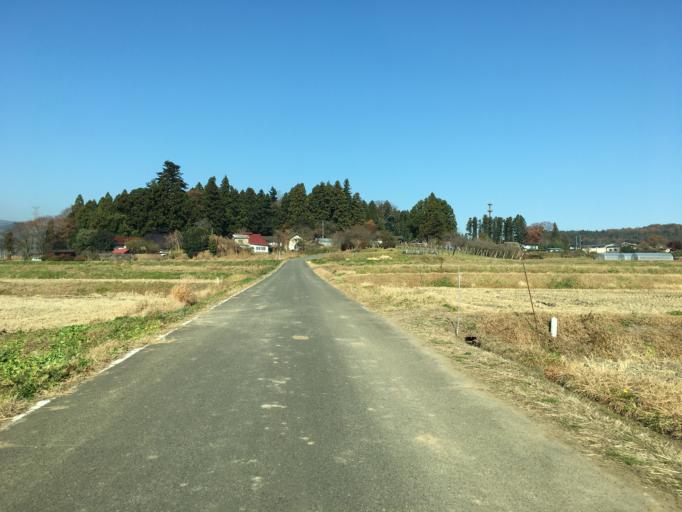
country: JP
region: Fukushima
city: Nihommatsu
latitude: 37.5772
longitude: 140.3901
